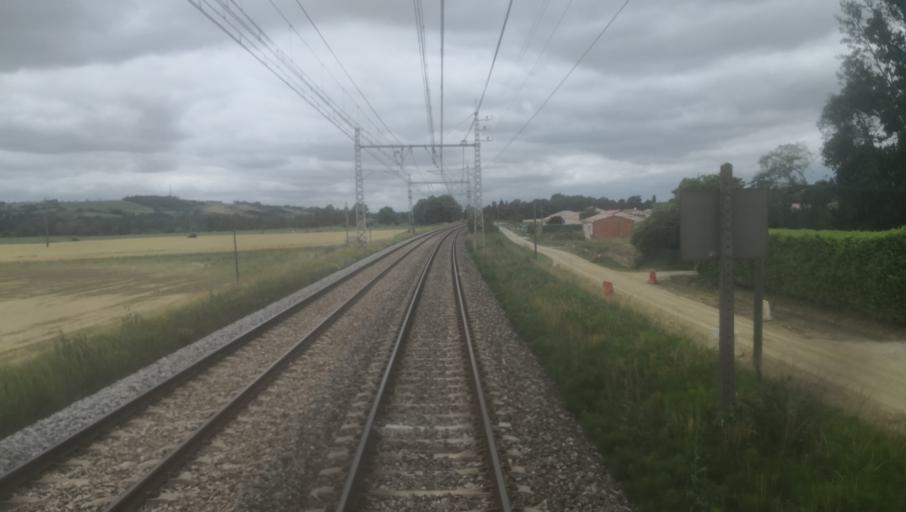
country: FR
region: Midi-Pyrenees
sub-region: Departement de la Haute-Garonne
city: Avignonet-Lauragais
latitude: 43.3669
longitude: 1.7758
